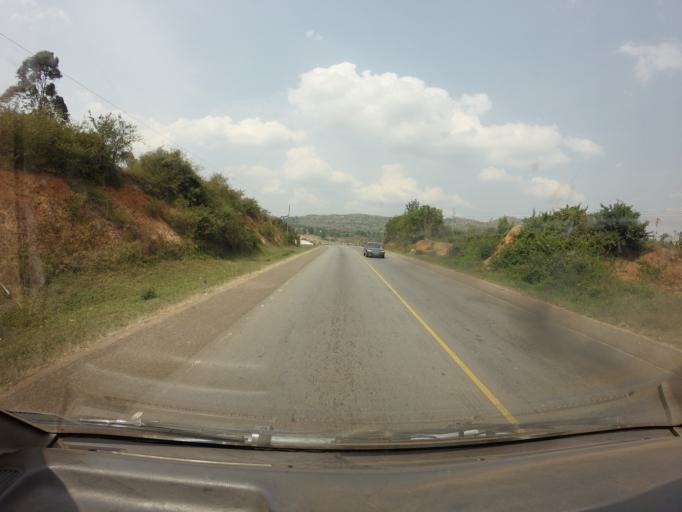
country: UG
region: Central Region
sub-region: Lyantonde District
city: Lyantonde
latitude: -0.3776
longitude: 31.2508
